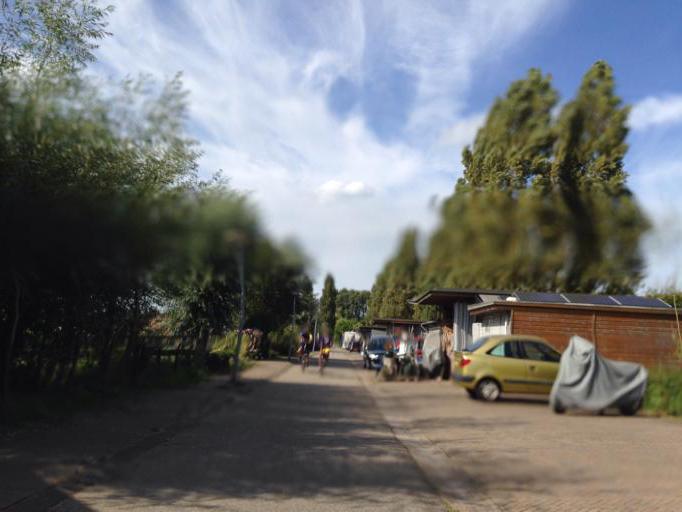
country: NL
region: Flevoland
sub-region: Gemeente Almere
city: Almere Stad
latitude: 52.3717
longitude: 5.2584
